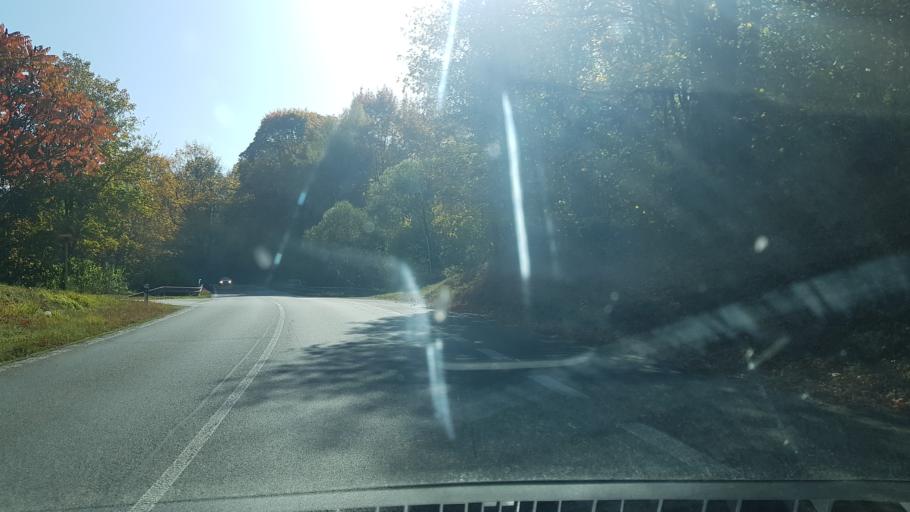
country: CZ
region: Jihocesky
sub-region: Okres Prachatice
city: Vimperk
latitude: 49.0667
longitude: 13.7816
